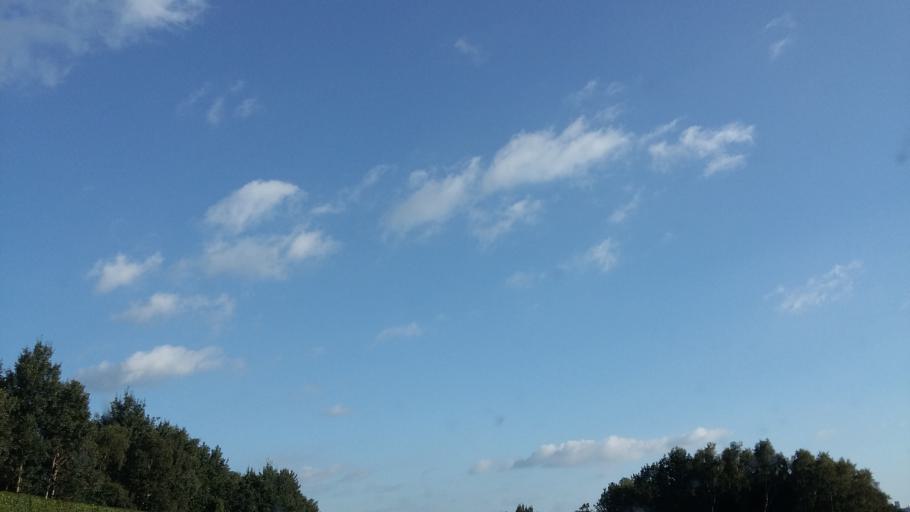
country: DE
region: Lower Saxony
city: Schiffdorf
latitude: 53.5288
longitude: 8.6228
